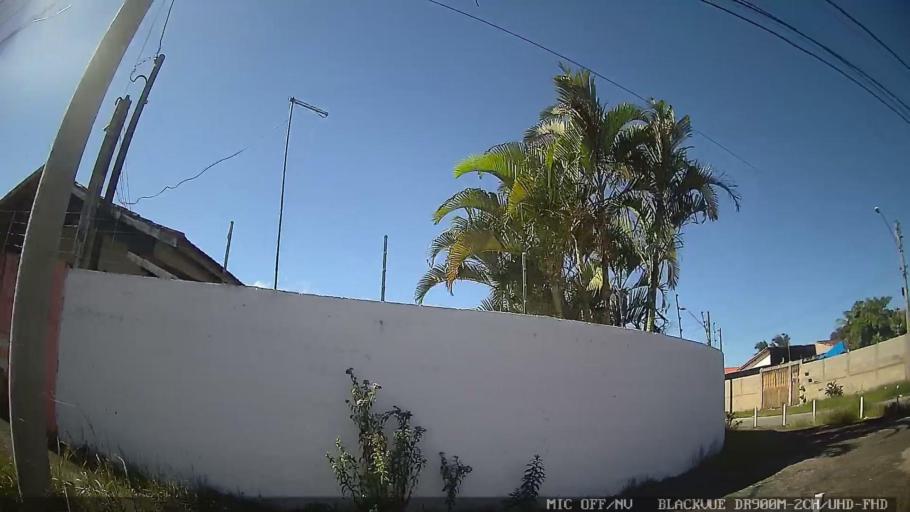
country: BR
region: Sao Paulo
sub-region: Itanhaem
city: Itanhaem
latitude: -24.2192
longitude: -46.8641
